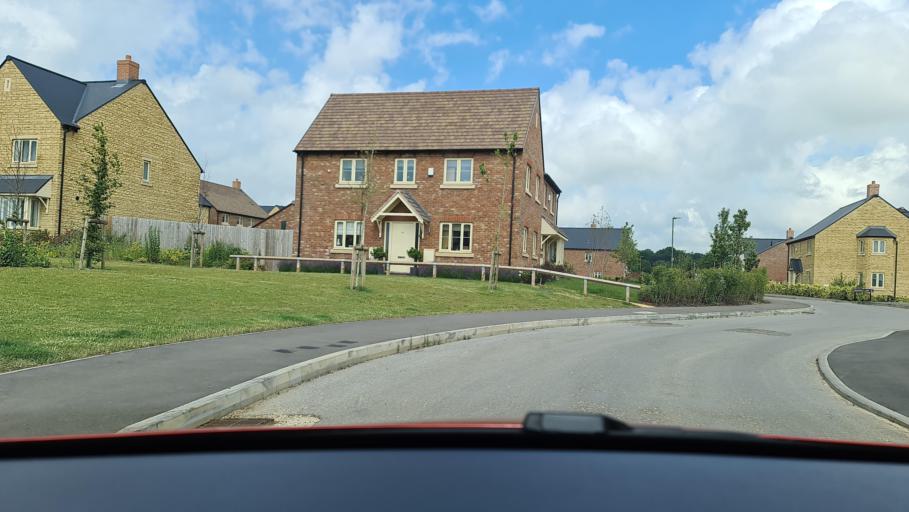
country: GB
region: England
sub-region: Oxfordshire
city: Stonesfield
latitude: 51.8228
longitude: -1.4028
